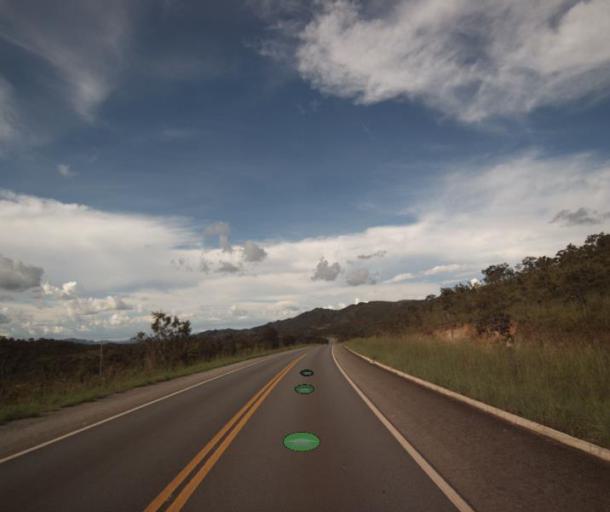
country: BR
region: Goias
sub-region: Barro Alto
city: Barro Alto
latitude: -15.0865
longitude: -48.7393
